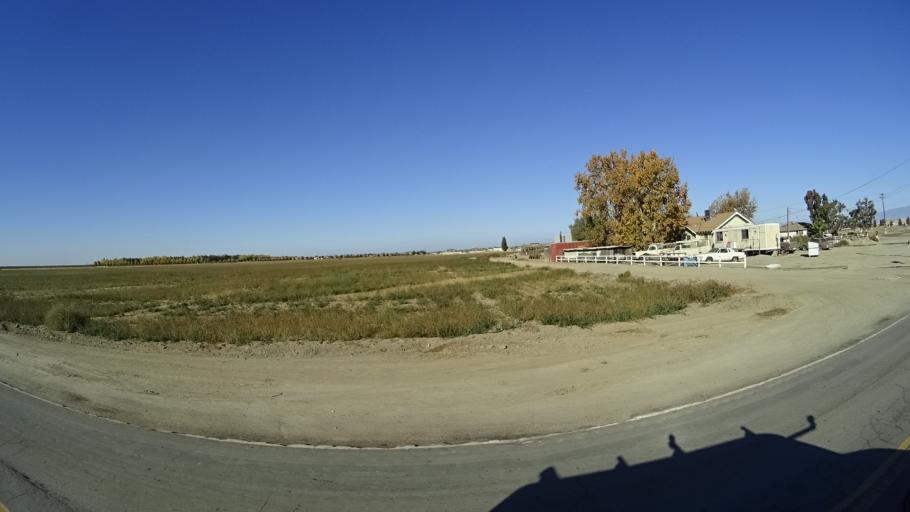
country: US
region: California
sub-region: Kern County
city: Greenacres
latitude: 35.2812
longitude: -119.1190
